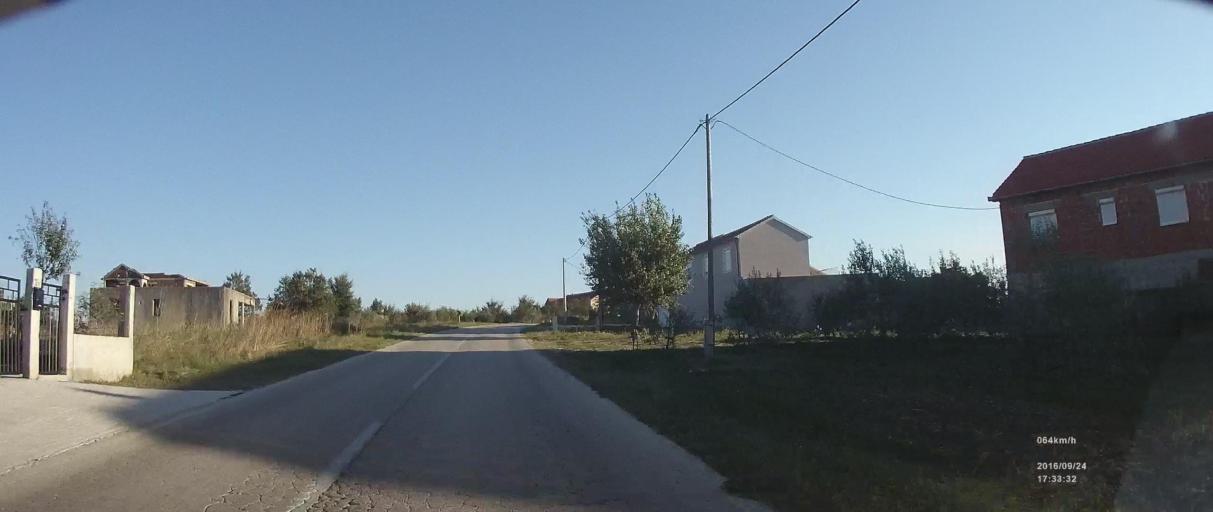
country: HR
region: Zadarska
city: Posedarje
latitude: 44.1735
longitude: 15.4574
